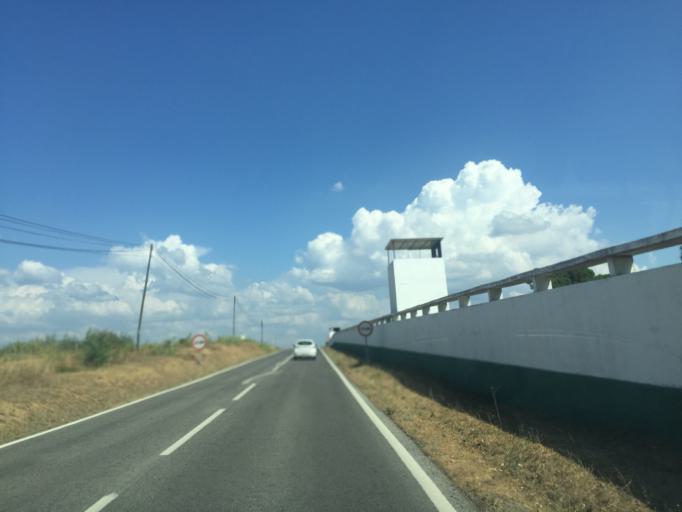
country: PT
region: Santarem
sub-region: Constancia
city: Constancia
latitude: 39.4714
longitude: -8.3752
